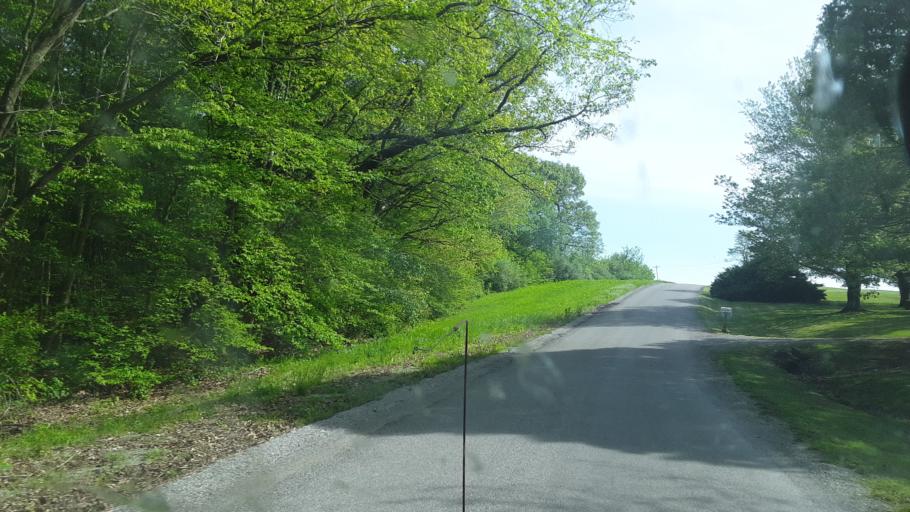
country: US
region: Illinois
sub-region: Jackson County
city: Carbondale
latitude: 37.6786
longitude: -89.2953
